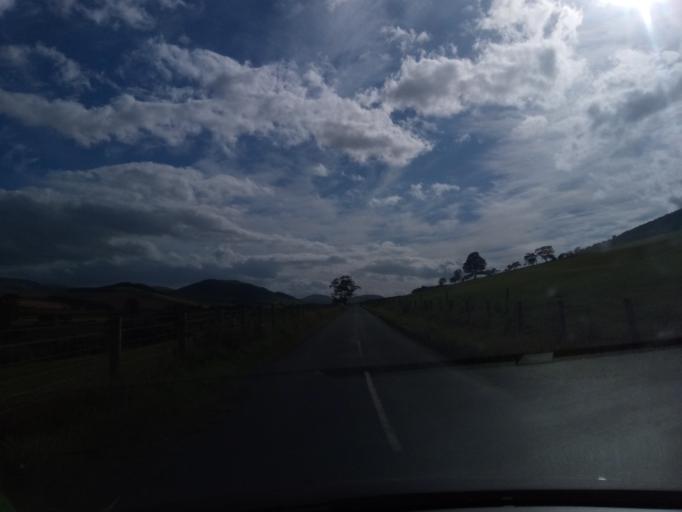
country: GB
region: Scotland
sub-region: The Scottish Borders
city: Coldstream
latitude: 55.5726
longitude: -2.2549
